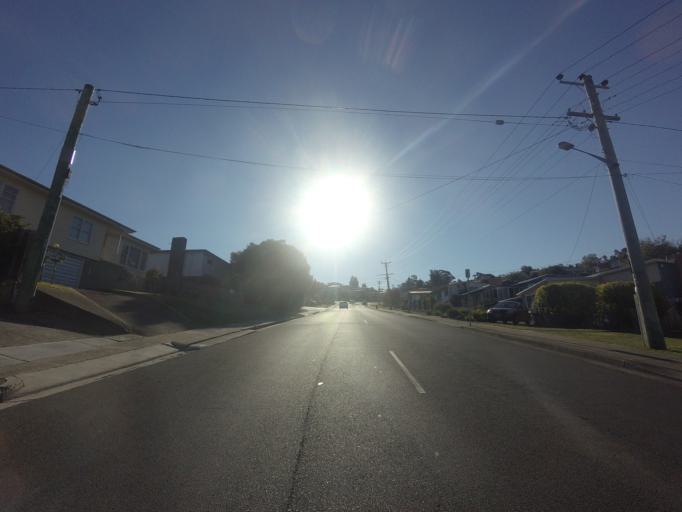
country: AU
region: Tasmania
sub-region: Glenorchy
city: West Moonah
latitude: -42.8622
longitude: 147.2811
